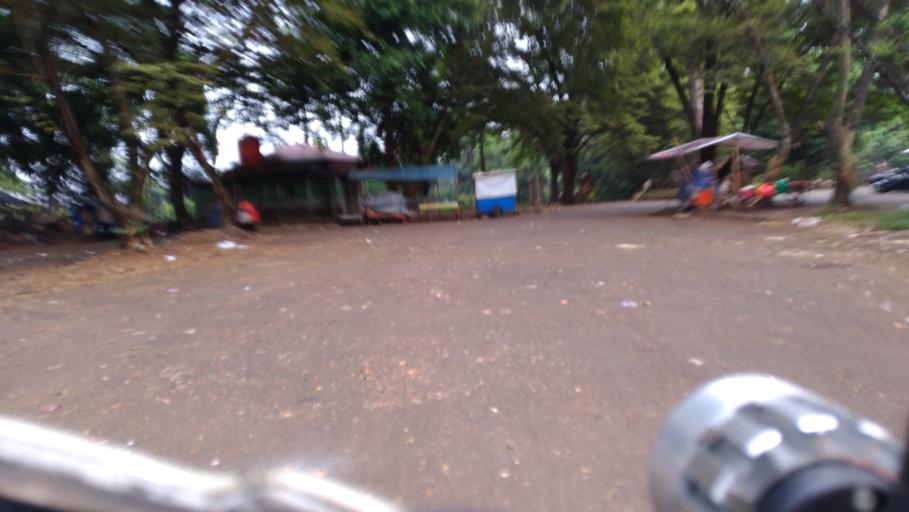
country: ID
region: West Java
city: Cileungsir
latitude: -6.3704
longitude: 106.9012
